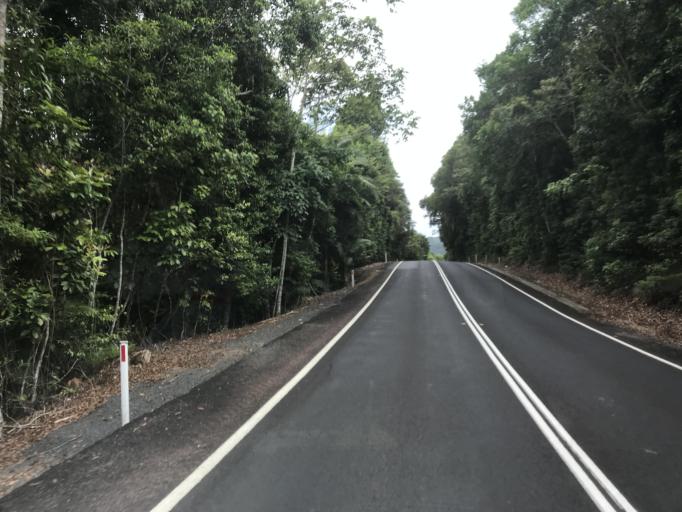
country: AU
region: Queensland
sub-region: Cassowary Coast
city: Innisfail
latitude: -17.8578
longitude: 146.0654
